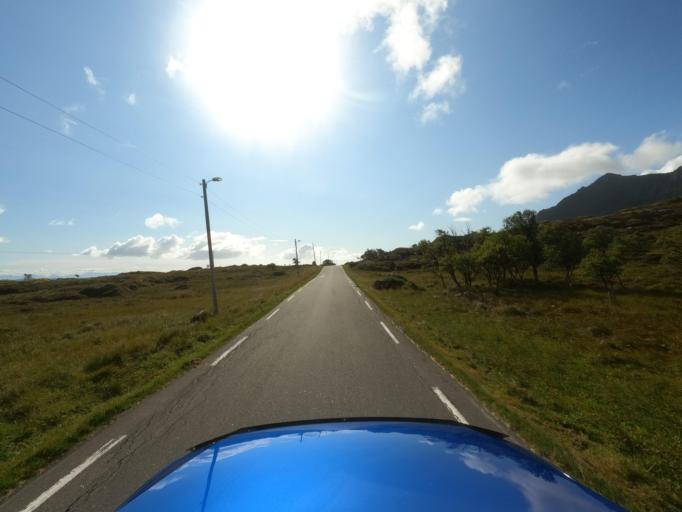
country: NO
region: Nordland
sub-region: Vestvagoy
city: Evjen
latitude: 68.2118
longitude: 14.0548
